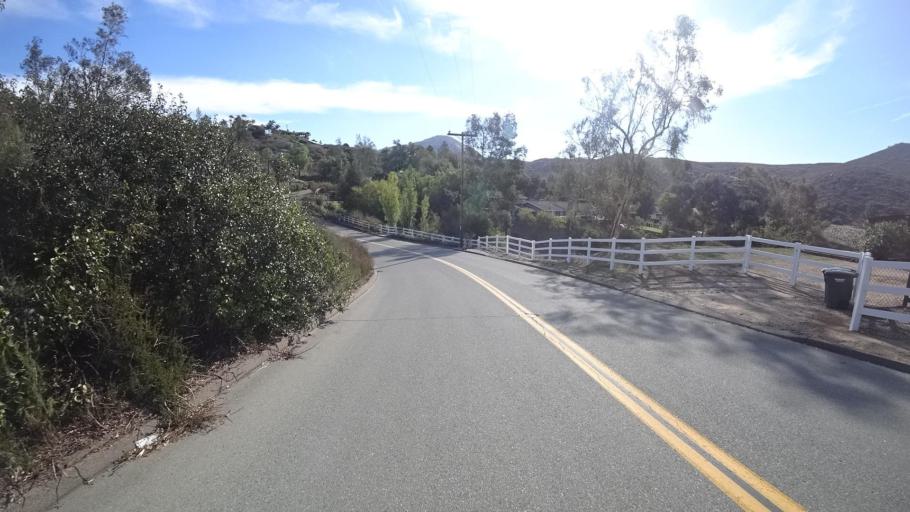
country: US
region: California
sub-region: San Diego County
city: Alpine
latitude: 32.8144
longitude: -116.7306
